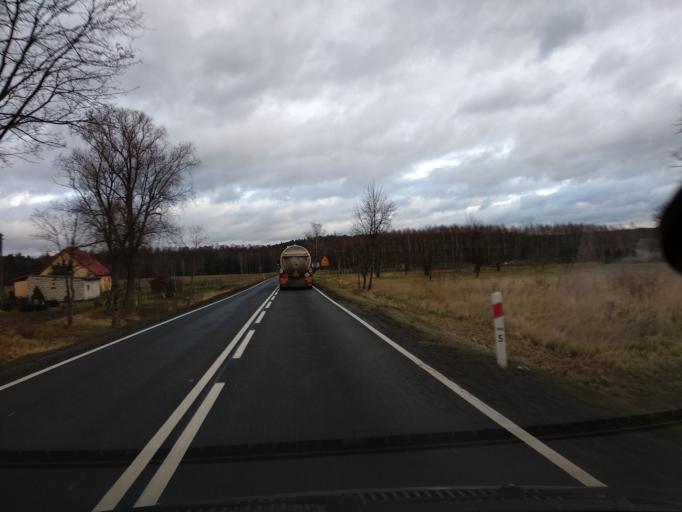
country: PL
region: Lower Silesian Voivodeship
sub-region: Powiat olesnicki
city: Miedzyborz
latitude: 51.3487
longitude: 17.5988
